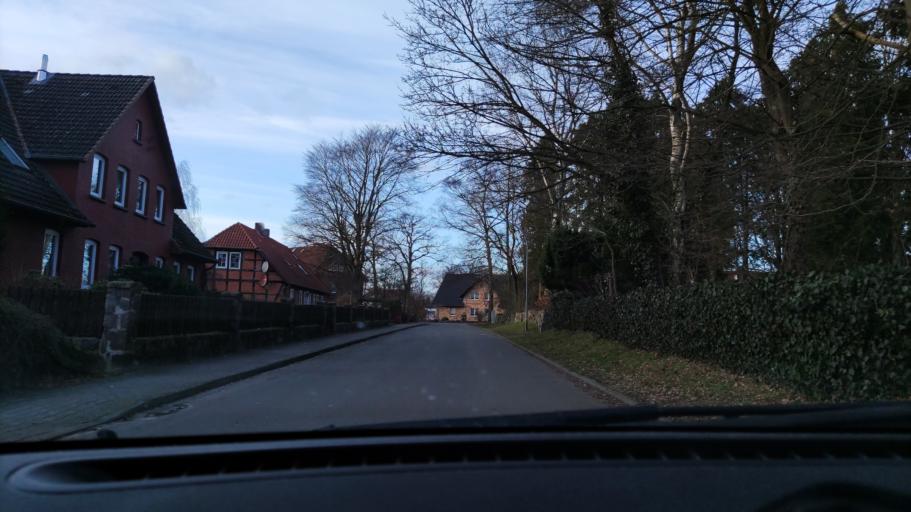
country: DE
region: Lower Saxony
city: Wriedel
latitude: 53.0318
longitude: 10.3030
